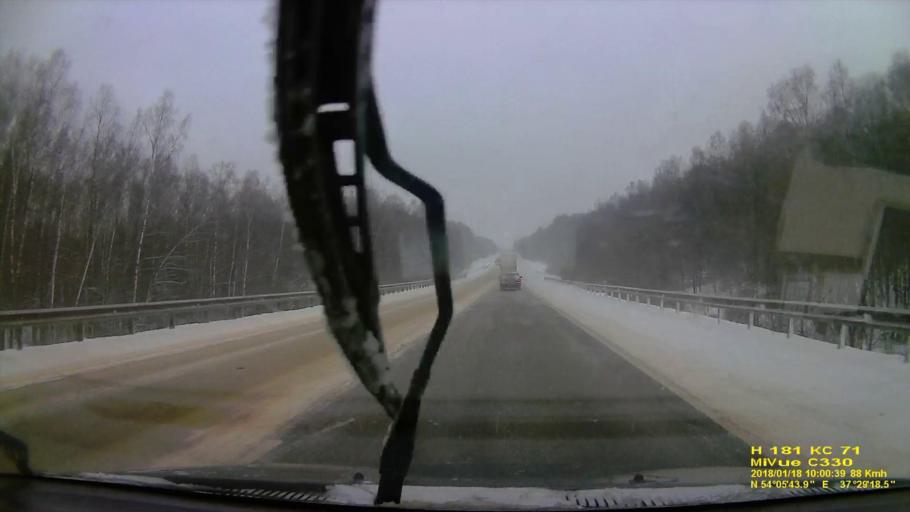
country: RU
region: Tula
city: Pervomayskiy
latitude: 54.0954
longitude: 37.4885
